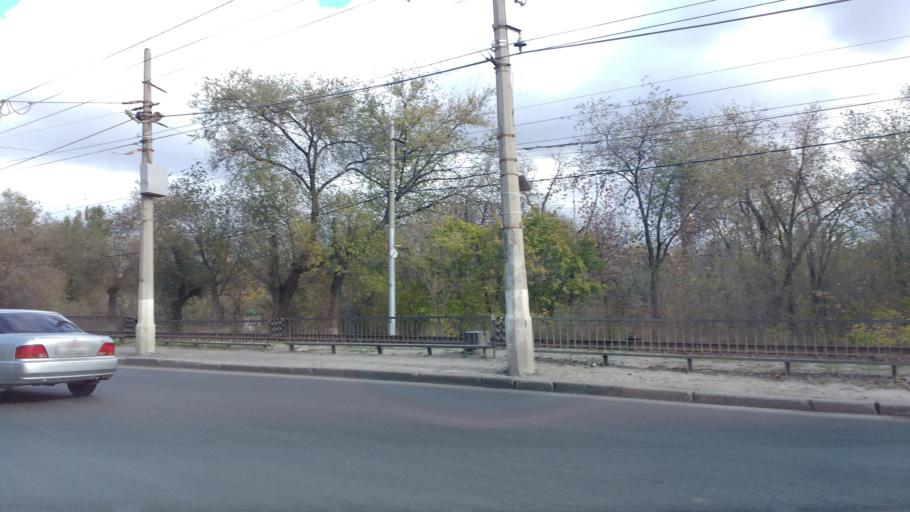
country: RU
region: Volgograd
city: Krasnoslobodsk
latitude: 48.7522
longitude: 44.5501
